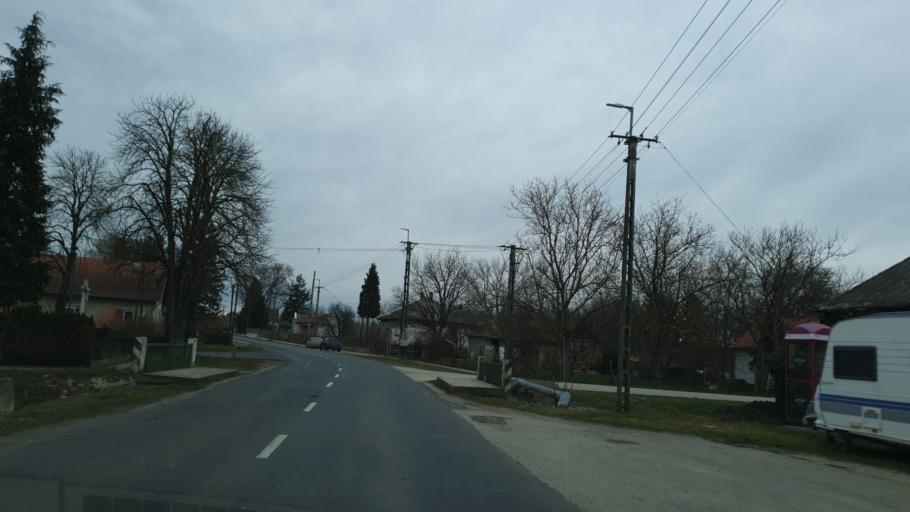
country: HU
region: Zala
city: Sarmellek
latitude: 46.7006
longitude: 17.1088
